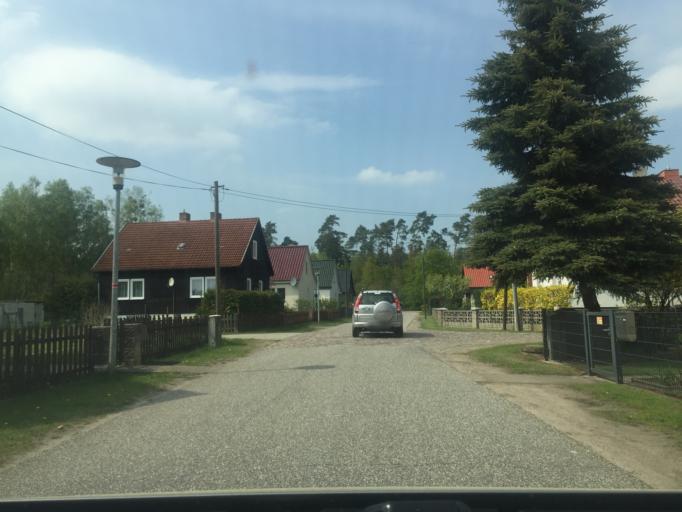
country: DE
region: Mecklenburg-Vorpommern
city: Torgelow
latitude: 53.6195
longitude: 14.0394
